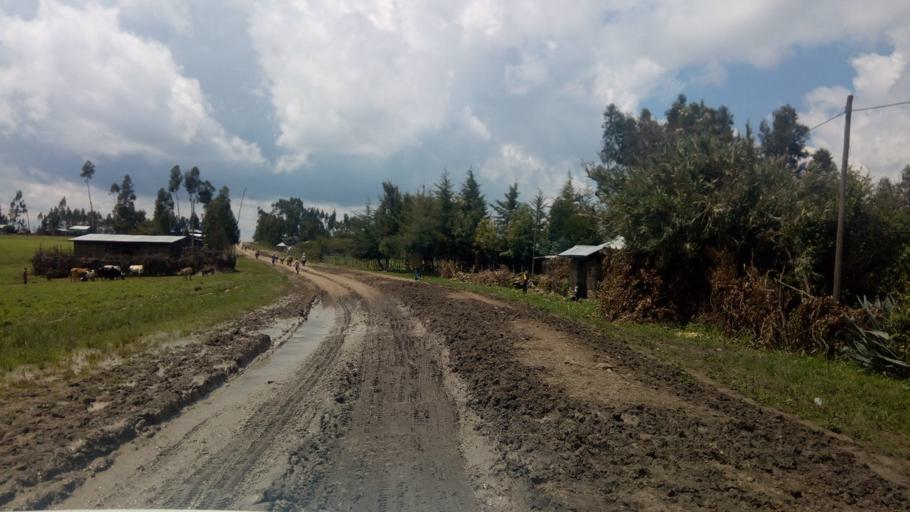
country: ET
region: Oromiya
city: Sendafa
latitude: 8.9982
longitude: 39.1275
